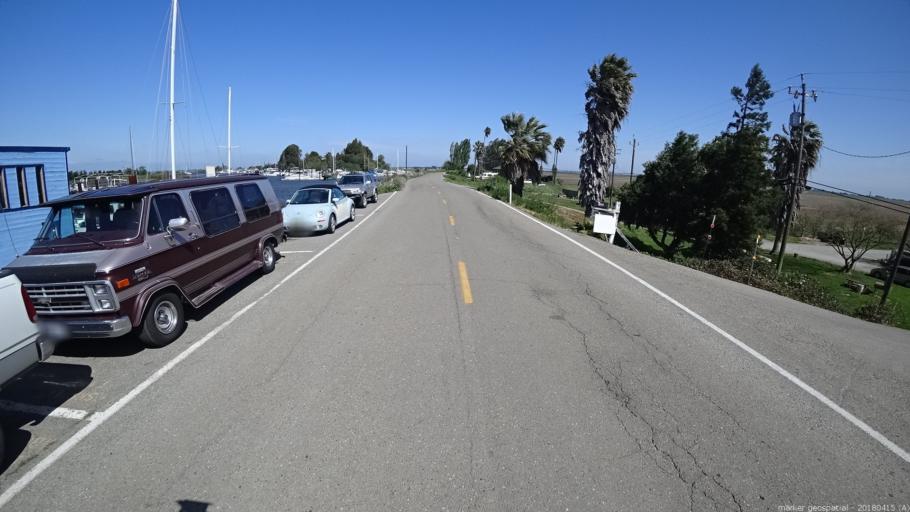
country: US
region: California
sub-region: Solano County
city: Rio Vista
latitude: 38.1113
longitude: -121.6138
